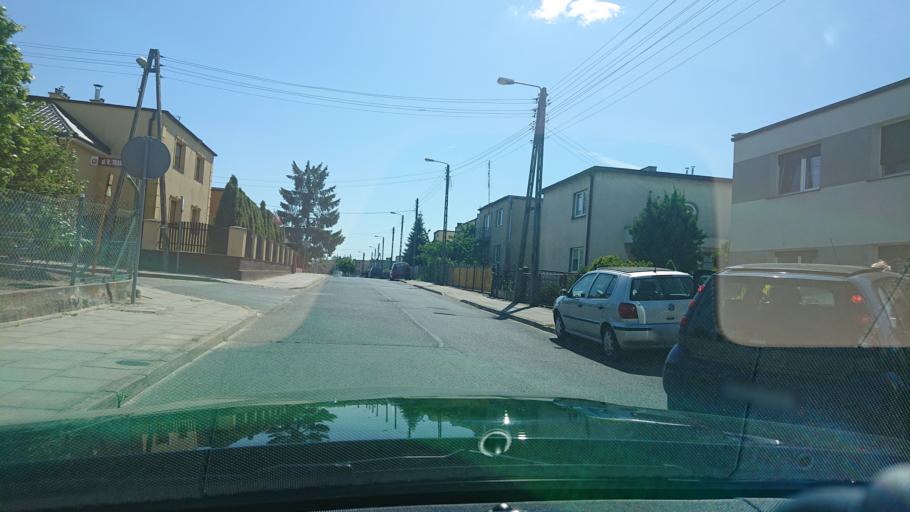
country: PL
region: Greater Poland Voivodeship
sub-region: Powiat gnieznienski
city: Gniezno
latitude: 52.5109
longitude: 17.5904
